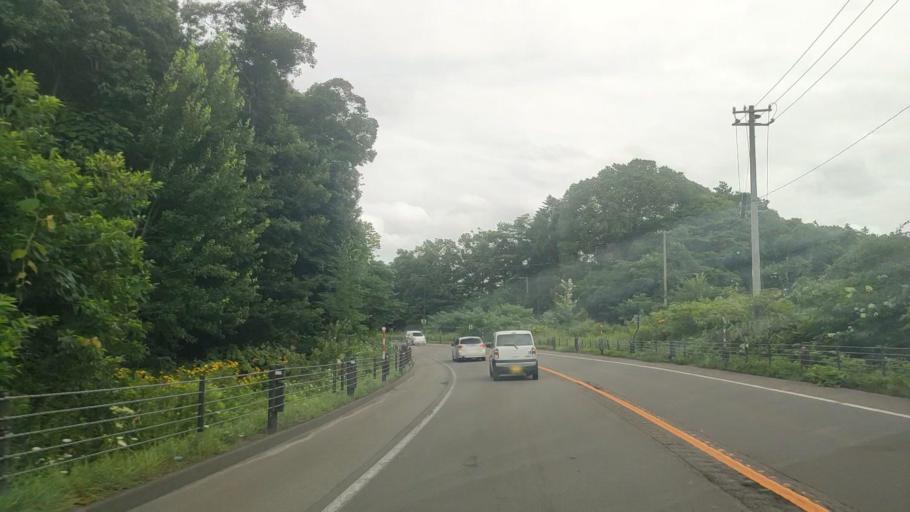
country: JP
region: Hokkaido
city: Nanae
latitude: 41.9687
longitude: 140.6508
